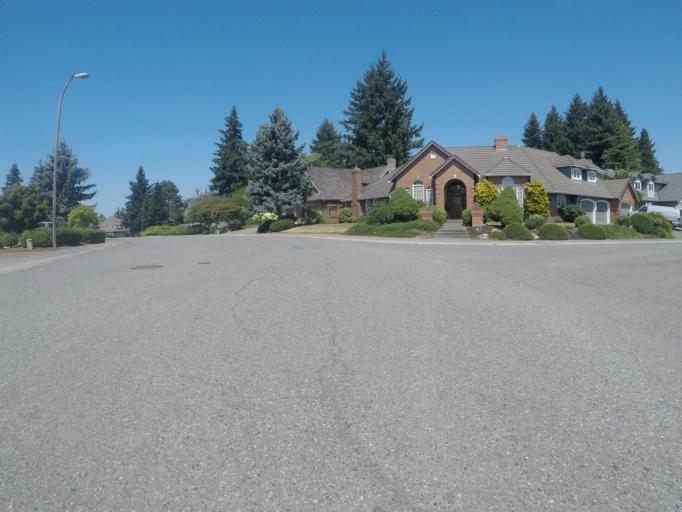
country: US
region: Washington
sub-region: King County
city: Kenmore
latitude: 47.7669
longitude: -122.2571
